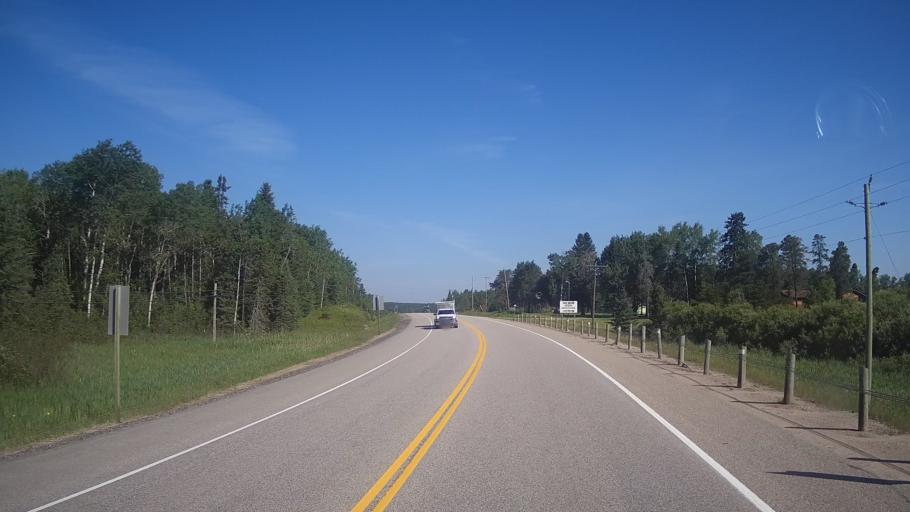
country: CA
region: Ontario
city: Dryden
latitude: 49.7314
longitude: -92.6107
